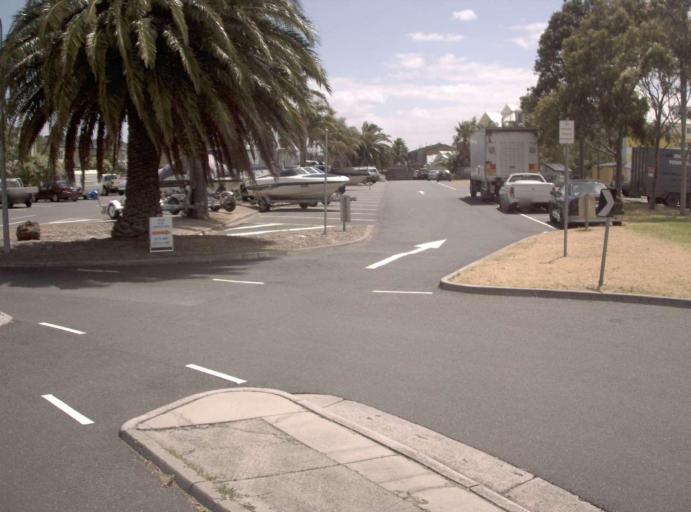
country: AU
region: Victoria
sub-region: Kingston
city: Patterson Lakes
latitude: -38.0696
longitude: 145.1405
